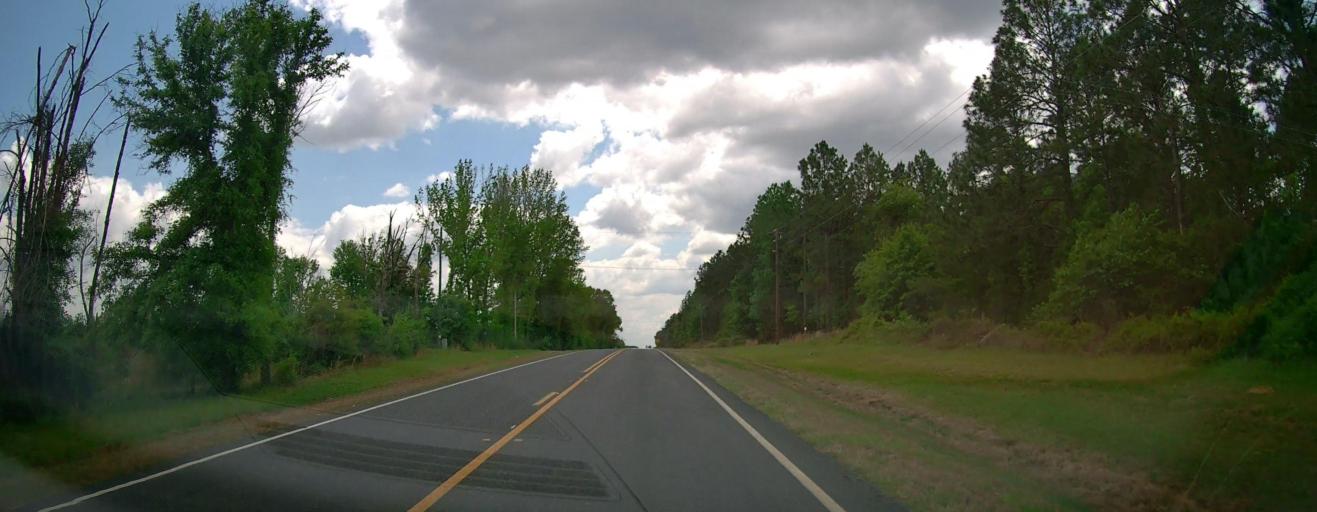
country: US
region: Georgia
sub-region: Treutlen County
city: Soperton
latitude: 32.4660
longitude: -82.6028
